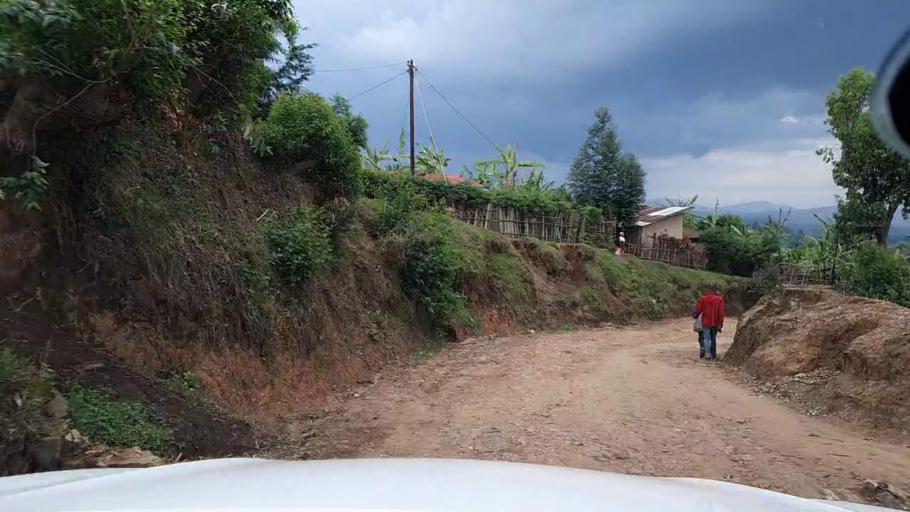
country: BI
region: Kayanza
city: Kayanza
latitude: -2.7918
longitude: 29.5184
